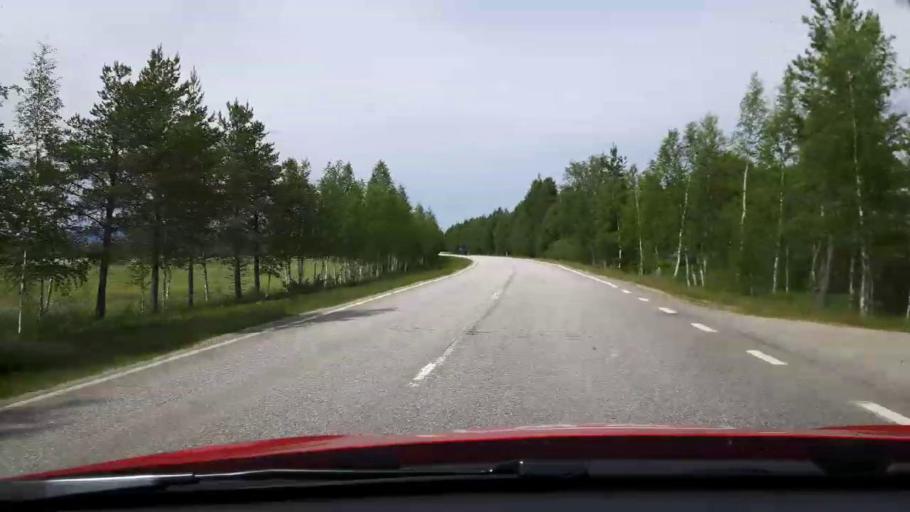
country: SE
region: Jaemtland
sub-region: Harjedalens Kommun
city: Sveg
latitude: 62.1278
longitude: 14.0662
